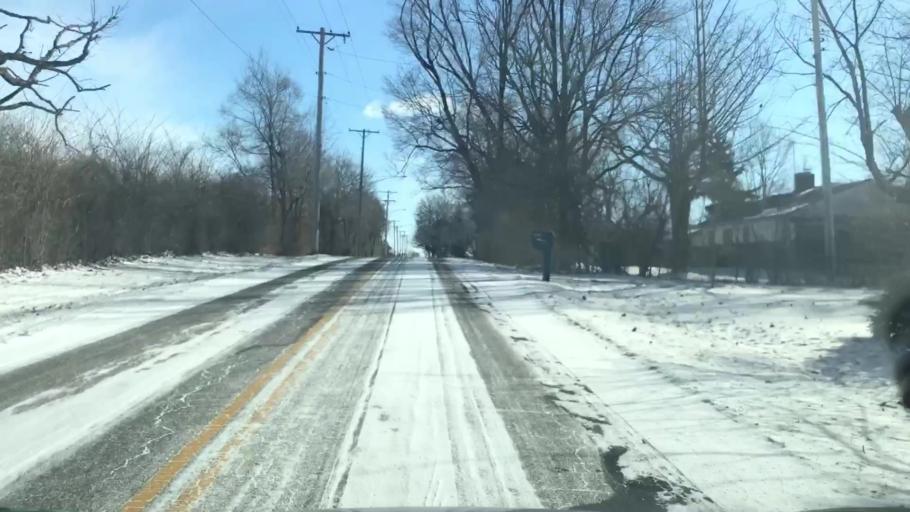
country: US
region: Ohio
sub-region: Greene County
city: Fairborn
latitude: 39.8405
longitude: -84.0112
